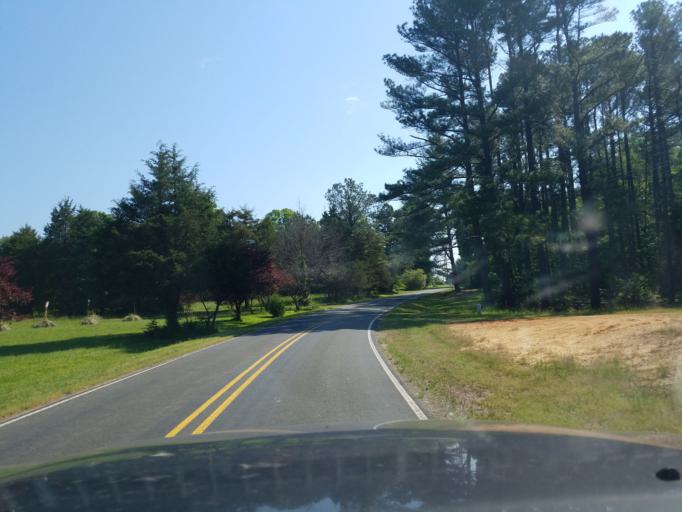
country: US
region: North Carolina
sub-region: Vance County
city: Henderson
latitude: 36.3929
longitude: -78.4406
